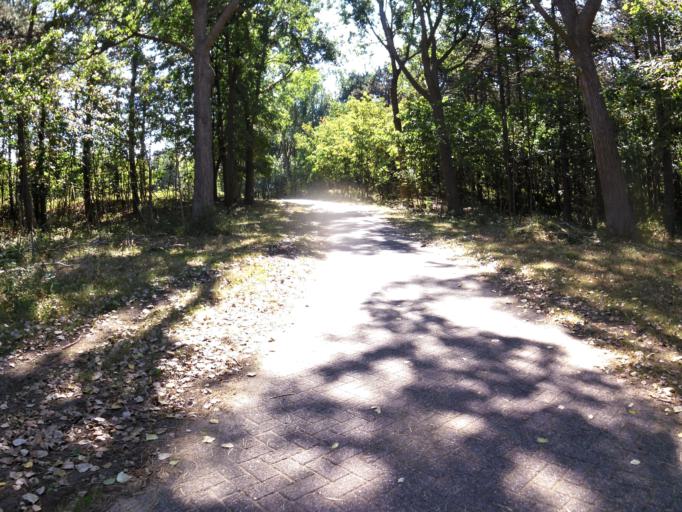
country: NL
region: North Holland
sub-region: Gemeente Beverwijk
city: Beverwijk
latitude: 52.5143
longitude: 4.6149
